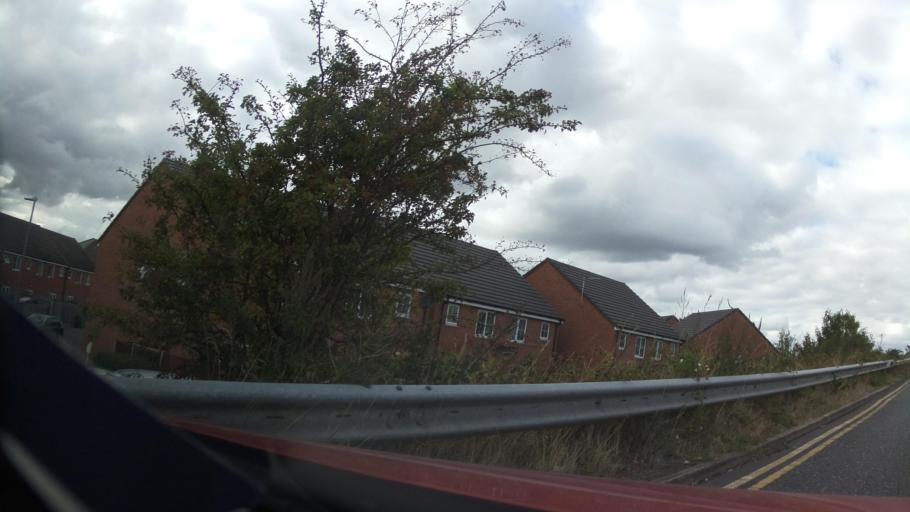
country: GB
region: England
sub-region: Leicestershire
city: Loughborough
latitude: 52.7816
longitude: -1.2016
